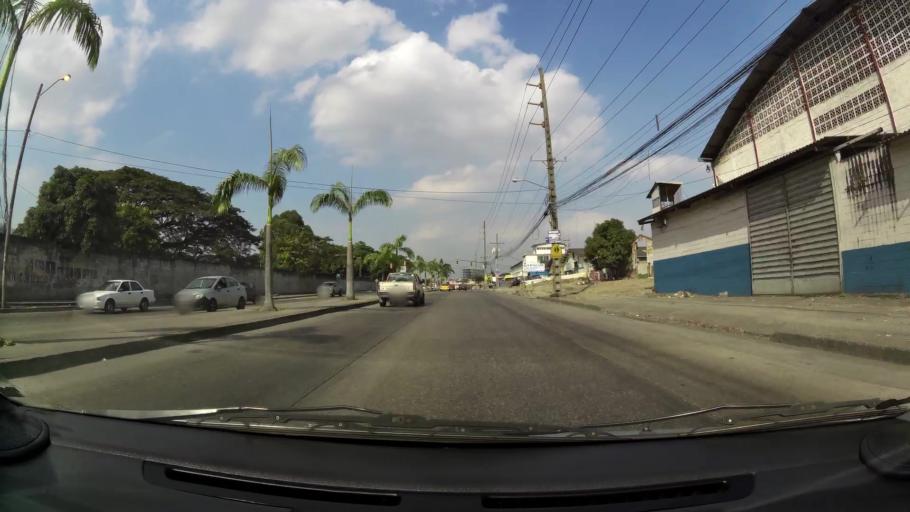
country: EC
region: Guayas
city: Guayaquil
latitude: -2.1307
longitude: -79.9322
